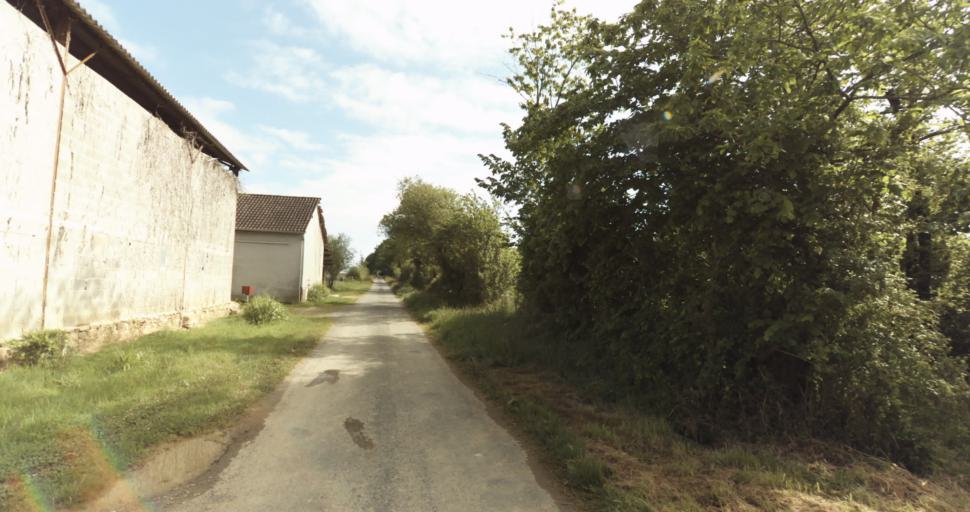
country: FR
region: Limousin
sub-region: Departement de la Haute-Vienne
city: Bosmie-l'Aiguille
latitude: 45.7139
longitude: 1.2360
